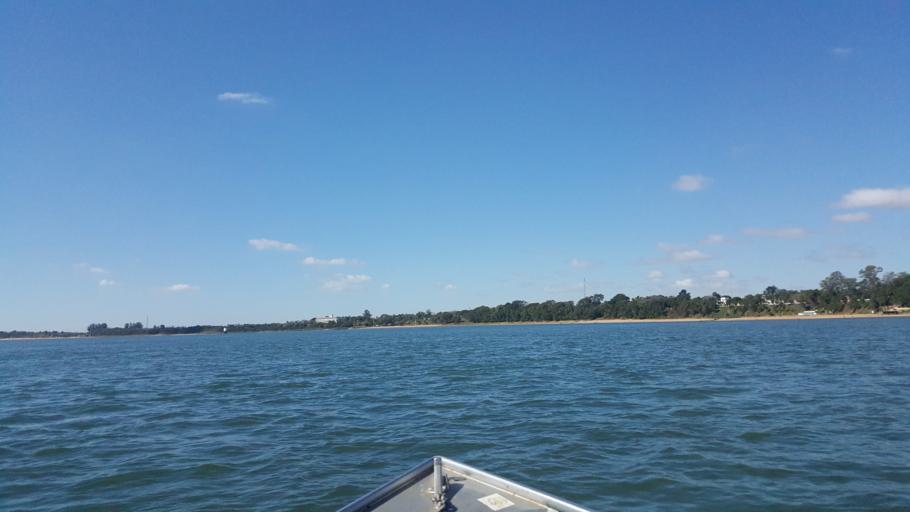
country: AR
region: Corrientes
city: Ituzaingo
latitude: -27.5812
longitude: -56.6946
